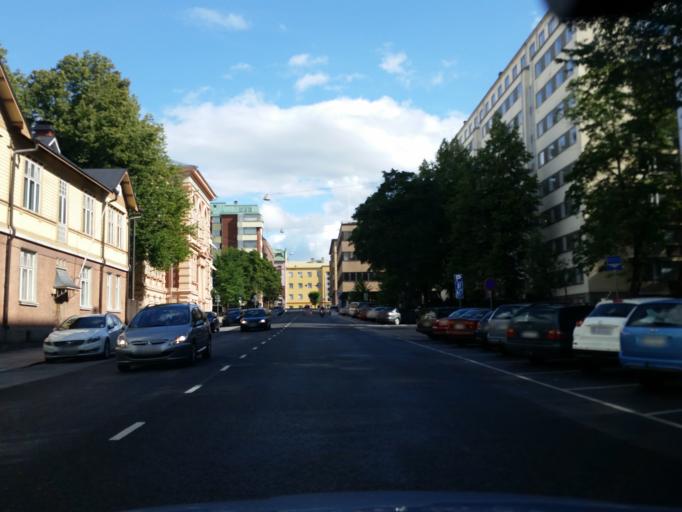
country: FI
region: Varsinais-Suomi
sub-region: Turku
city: Turku
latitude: 60.4519
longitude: 22.2595
